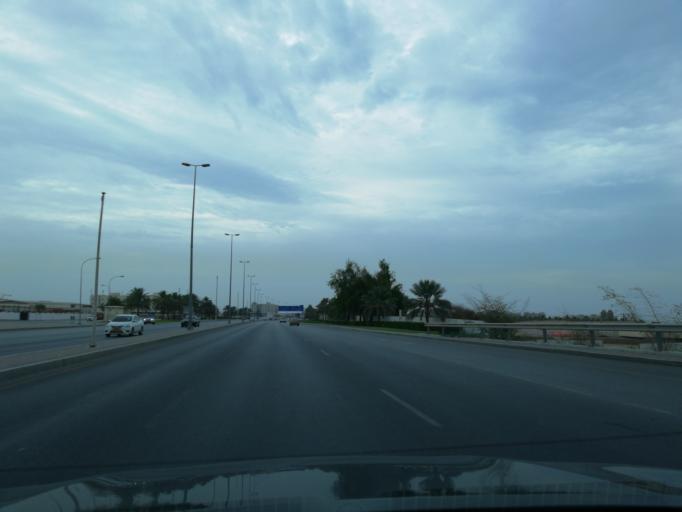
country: OM
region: Muhafazat Masqat
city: Bawshar
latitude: 23.5774
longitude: 58.3825
